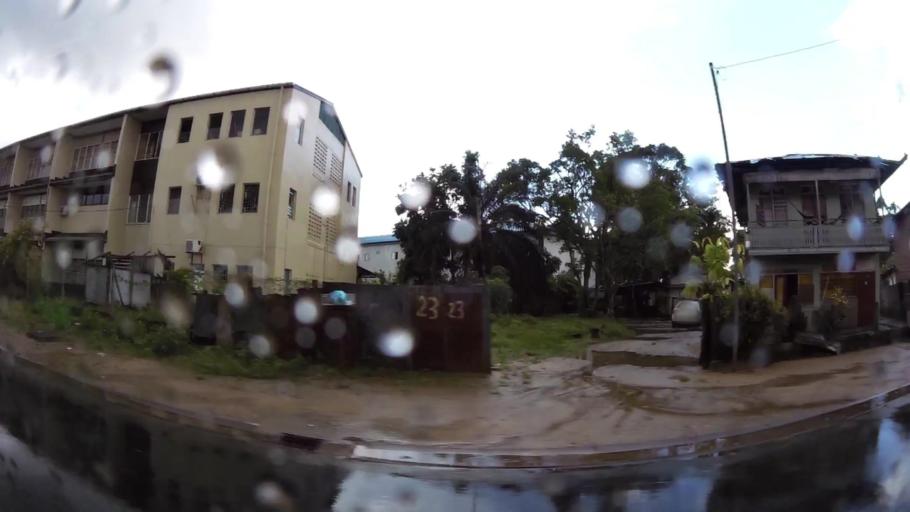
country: SR
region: Paramaribo
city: Paramaribo
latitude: 5.8243
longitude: -55.1702
